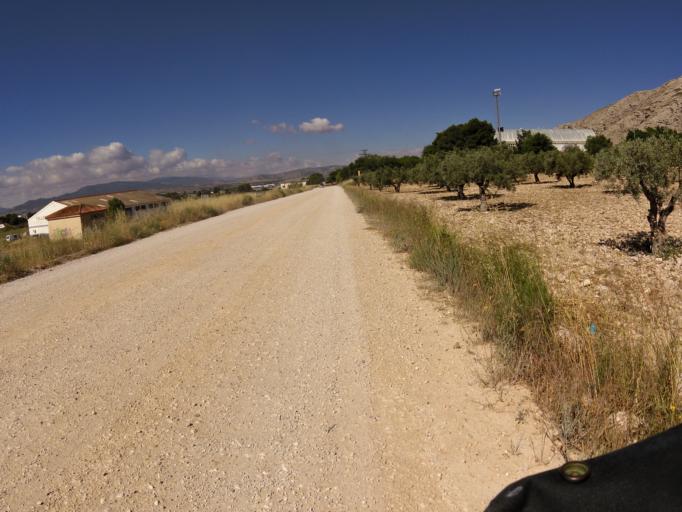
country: ES
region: Valencia
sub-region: Provincia de Alicante
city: Villena
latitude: 38.6321
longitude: -0.8436
